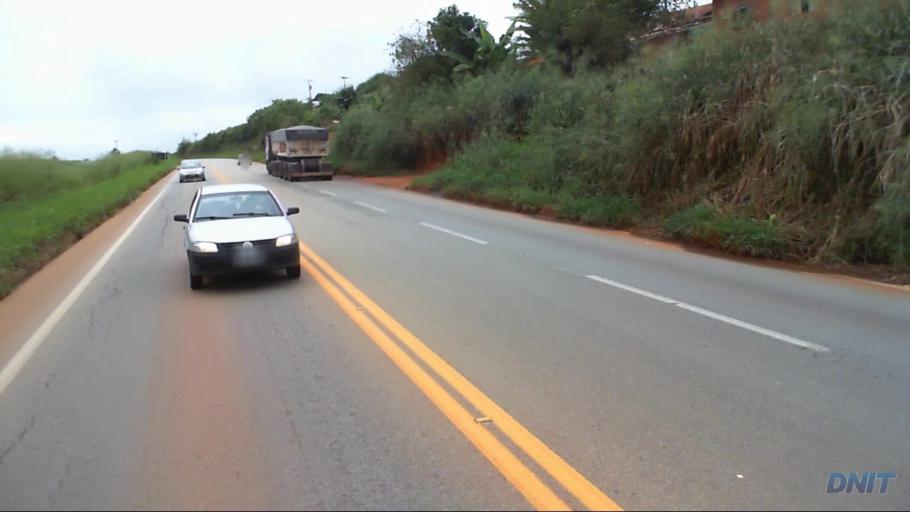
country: BR
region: Minas Gerais
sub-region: Nova Era
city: Nova Era
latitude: -19.8139
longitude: -43.0656
